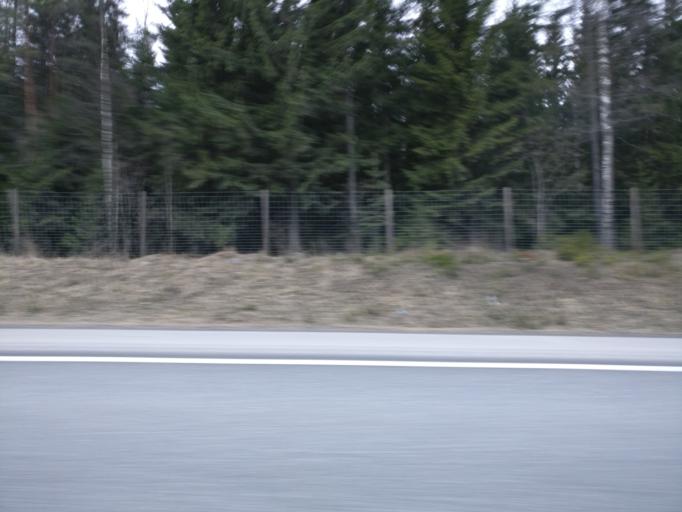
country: FI
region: Haeme
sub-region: Haemeenlinna
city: Tervakoski
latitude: 60.8020
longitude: 24.6836
